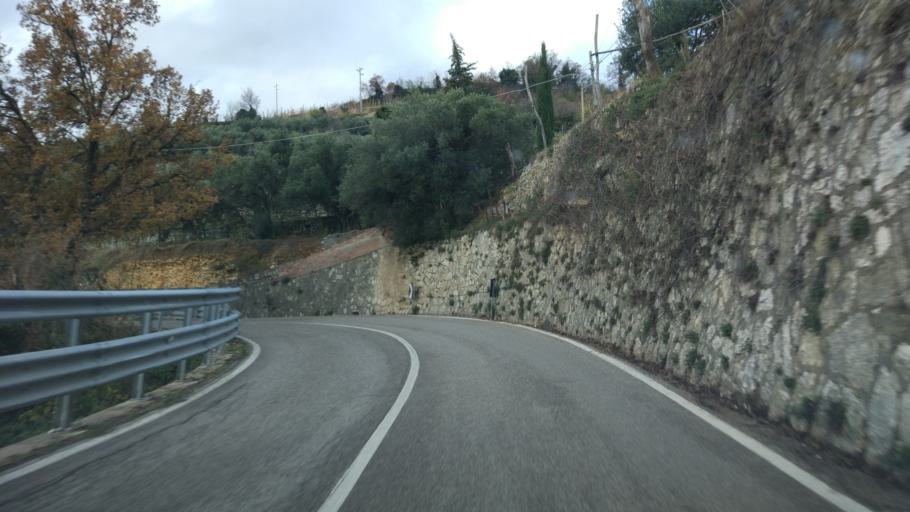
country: IT
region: Veneto
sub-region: Provincia di Verona
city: Marano di Valpolicella
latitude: 45.5539
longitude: 10.9125
